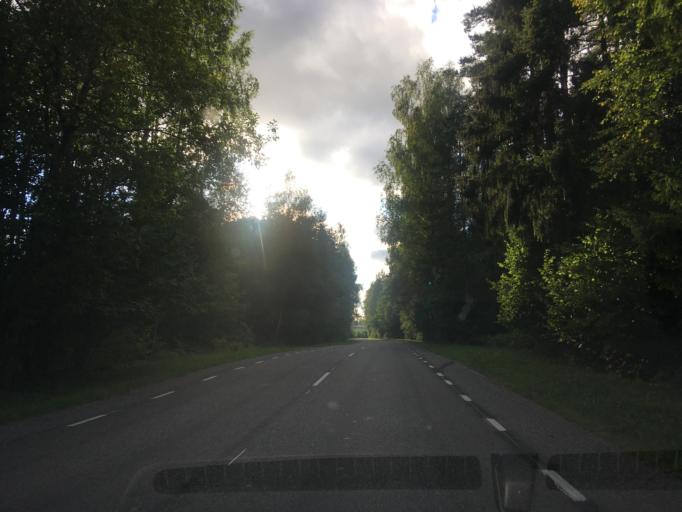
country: EE
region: Raplamaa
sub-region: Maerjamaa vald
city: Marjamaa
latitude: 58.8974
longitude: 24.4506
